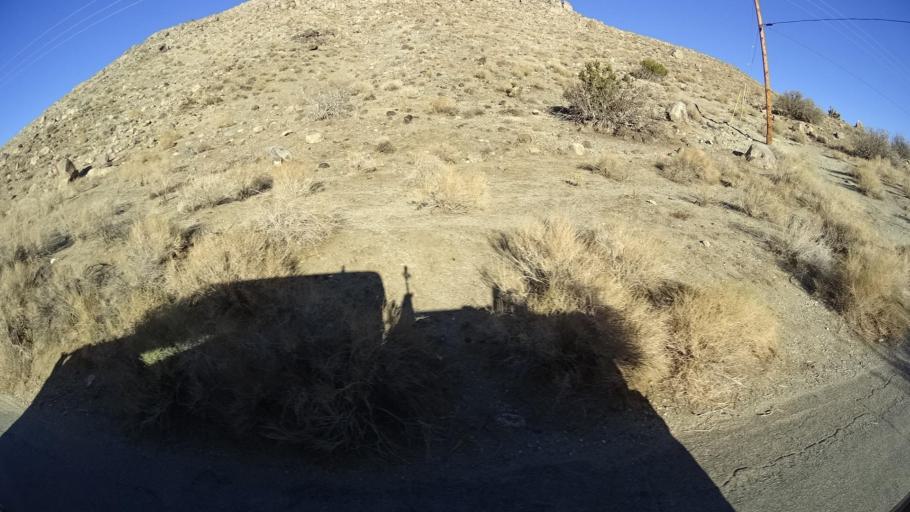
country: US
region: California
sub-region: Kern County
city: Weldon
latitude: 35.5662
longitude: -118.2469
